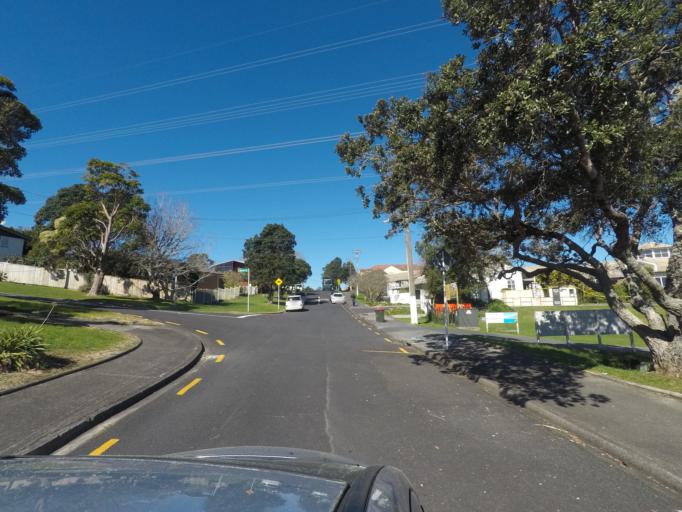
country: NZ
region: Auckland
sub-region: Auckland
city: Waitakere
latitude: -36.9300
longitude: 174.6963
